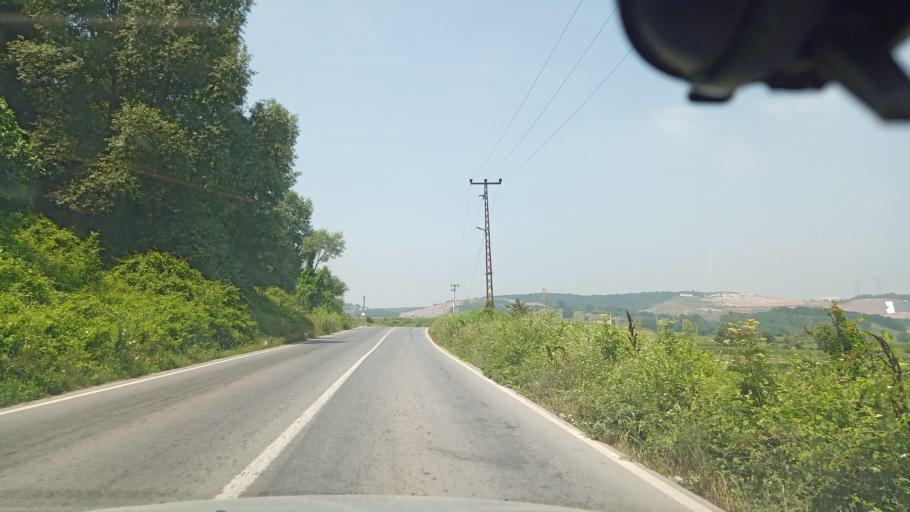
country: TR
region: Sakarya
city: Adapazari
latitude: 40.8306
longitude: 30.3989
